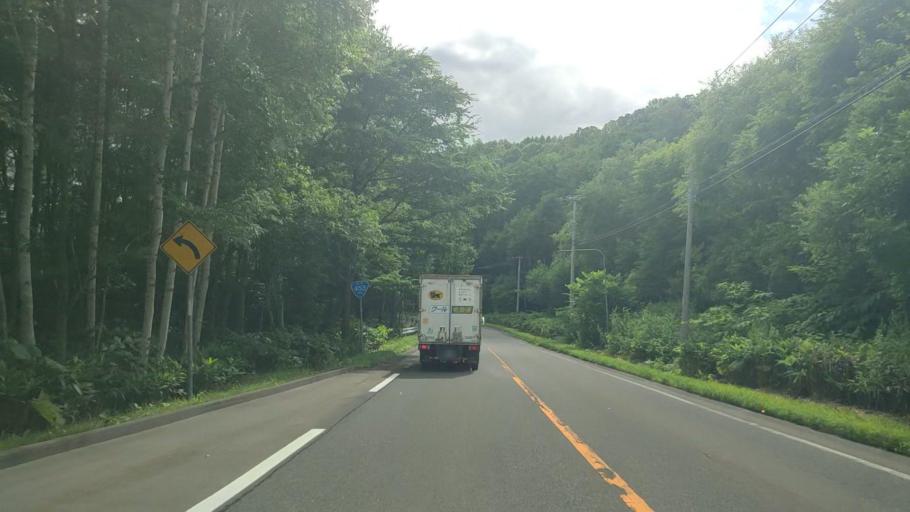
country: JP
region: Hokkaido
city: Date
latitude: 42.6608
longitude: 141.0697
